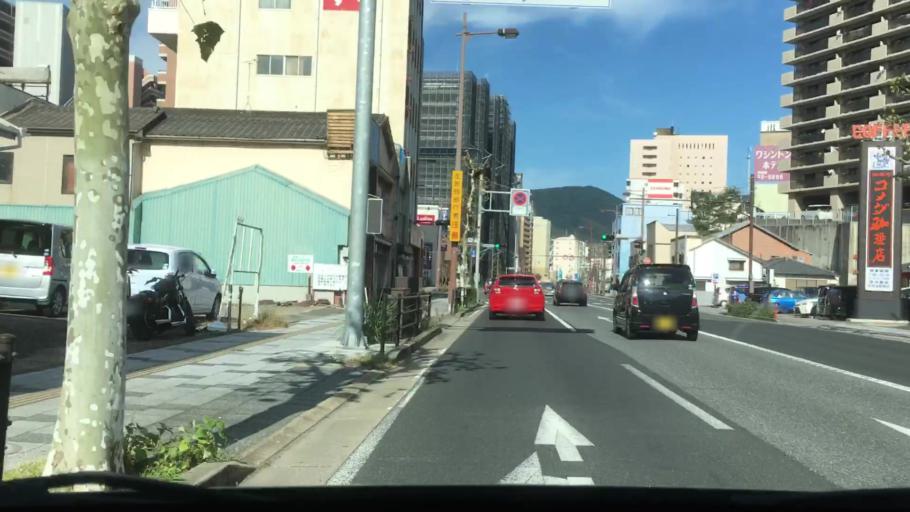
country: JP
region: Nagasaki
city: Sasebo
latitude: 33.1619
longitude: 129.7299
